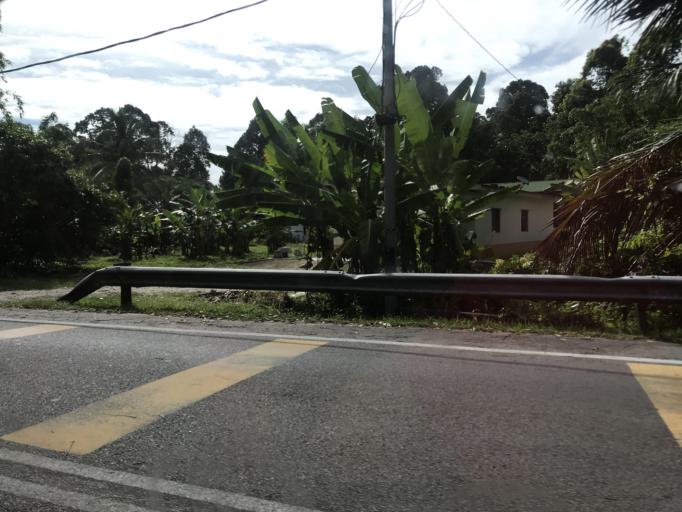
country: MY
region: Kelantan
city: Kota Bharu
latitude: 6.1306
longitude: 102.1760
